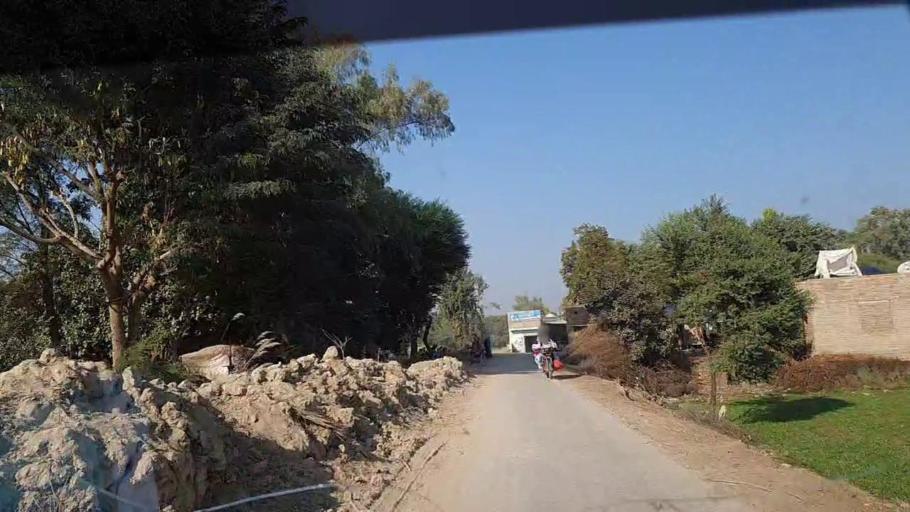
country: PK
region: Sindh
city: Sobhadero
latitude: 27.2531
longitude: 68.3290
